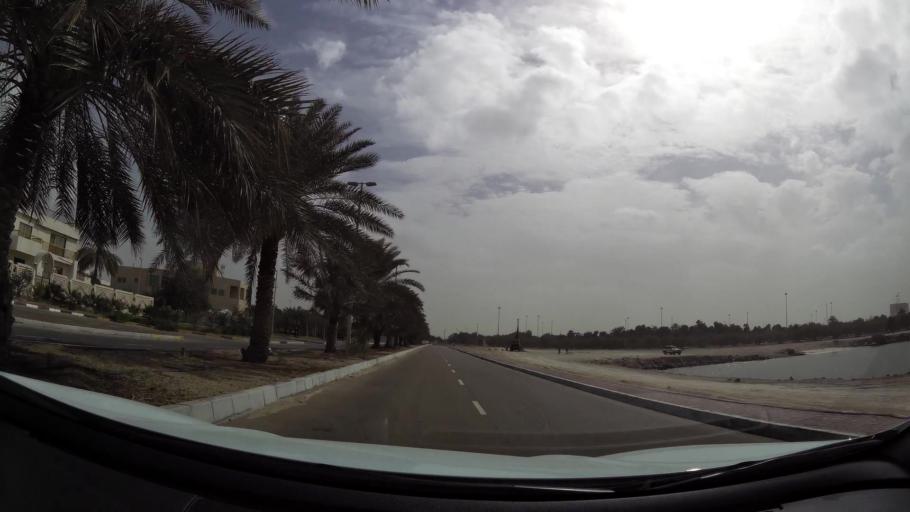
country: AE
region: Abu Dhabi
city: Abu Dhabi
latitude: 24.3973
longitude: 54.5198
